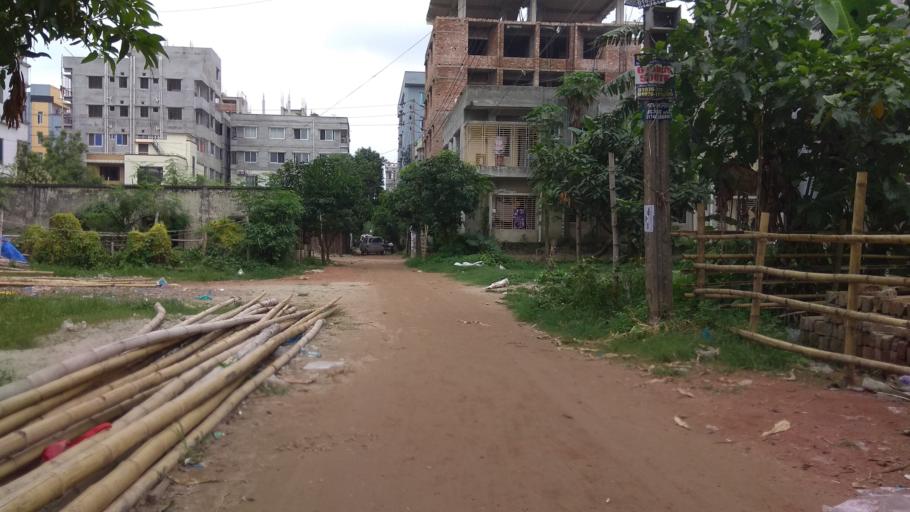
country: BD
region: Dhaka
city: Tungi
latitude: 23.8213
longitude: 90.3525
